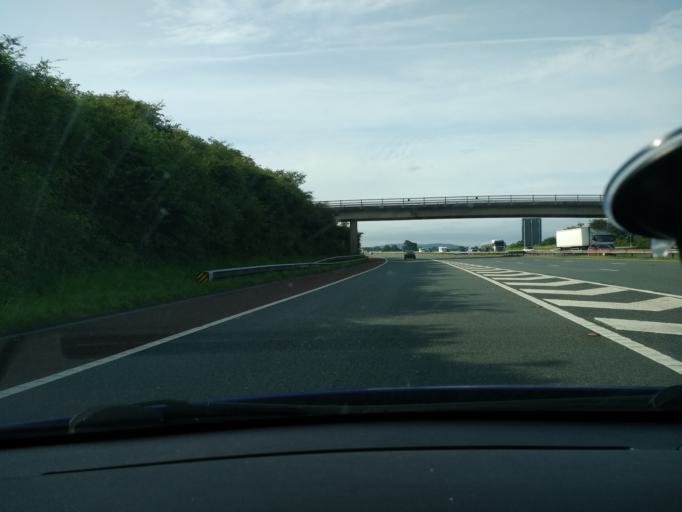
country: GB
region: England
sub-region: Cumbria
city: Milnthorpe
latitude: 54.2334
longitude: -2.7194
